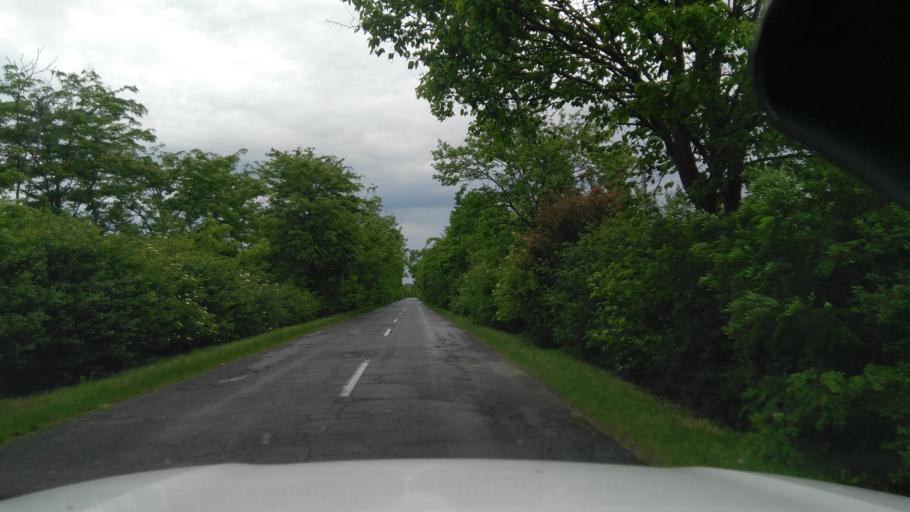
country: HU
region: Bekes
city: Bekescsaba
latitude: 46.6927
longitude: 21.1692
